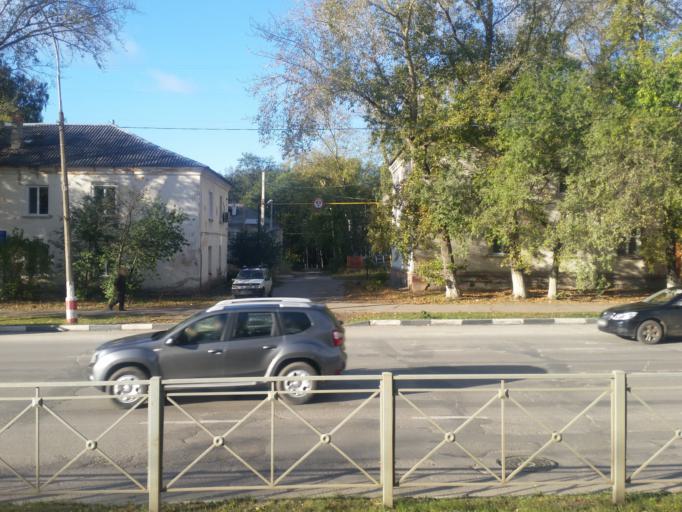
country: RU
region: Ulyanovsk
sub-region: Ulyanovskiy Rayon
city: Ulyanovsk
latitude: 54.3411
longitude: 48.3783
